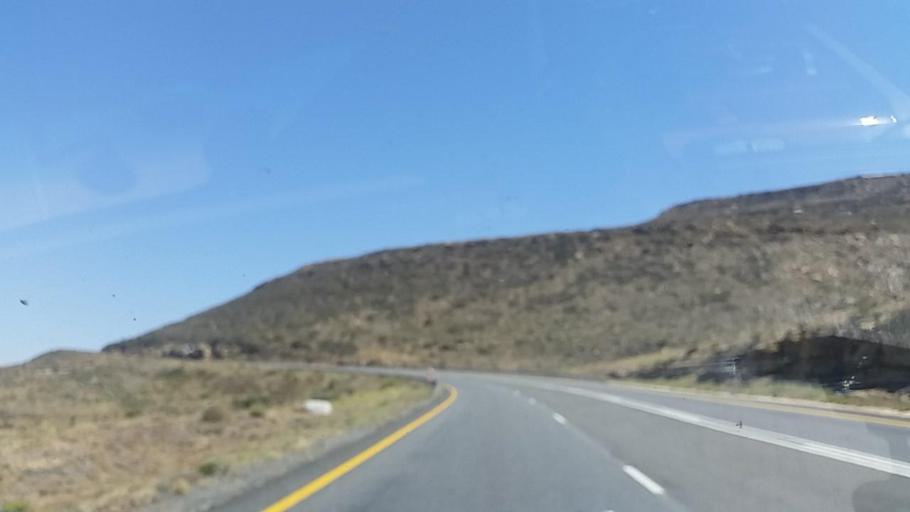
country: ZA
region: Eastern Cape
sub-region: Chris Hani District Municipality
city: Middelburg
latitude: -31.8445
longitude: 24.8778
